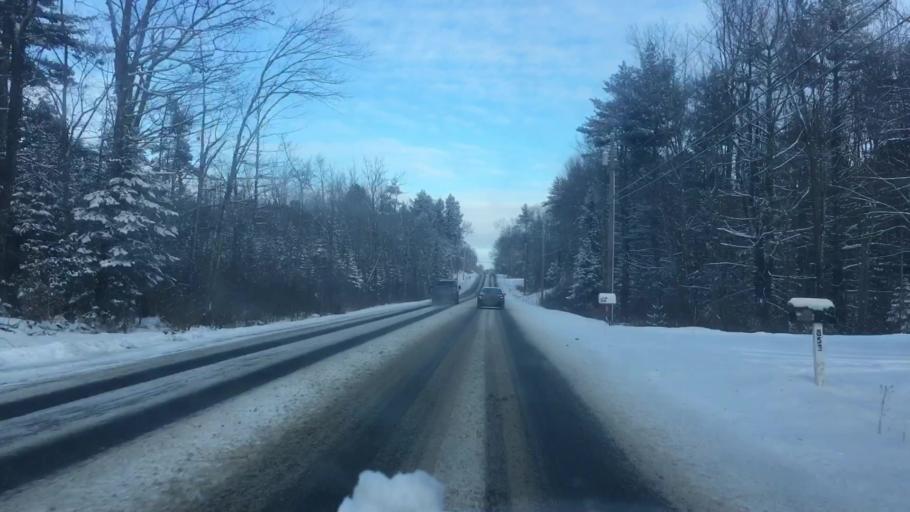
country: US
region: Maine
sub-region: Cumberland County
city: North Windham
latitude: 43.8031
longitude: -70.4404
